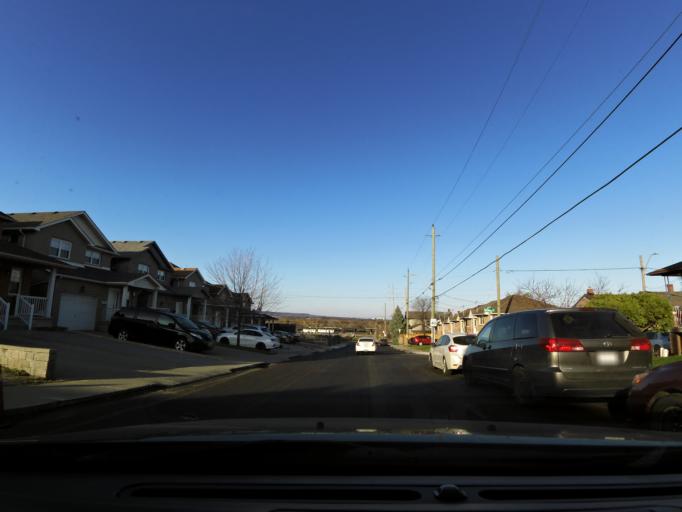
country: CA
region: Ontario
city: Hamilton
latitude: 43.2652
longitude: -79.8746
